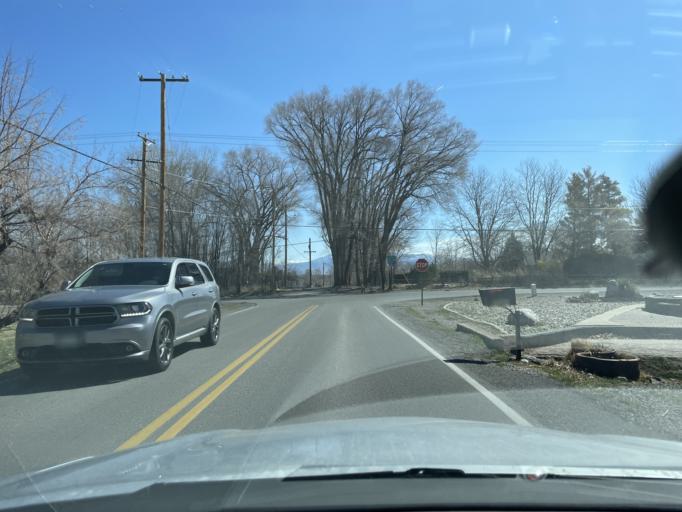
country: US
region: Colorado
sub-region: Mesa County
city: Redlands
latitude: 39.0850
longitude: -108.6693
